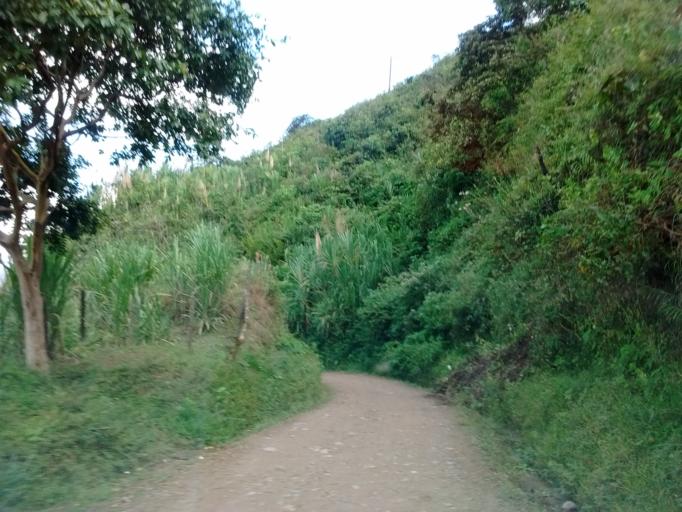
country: CO
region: Cauca
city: Morales
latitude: 2.6874
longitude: -76.7350
